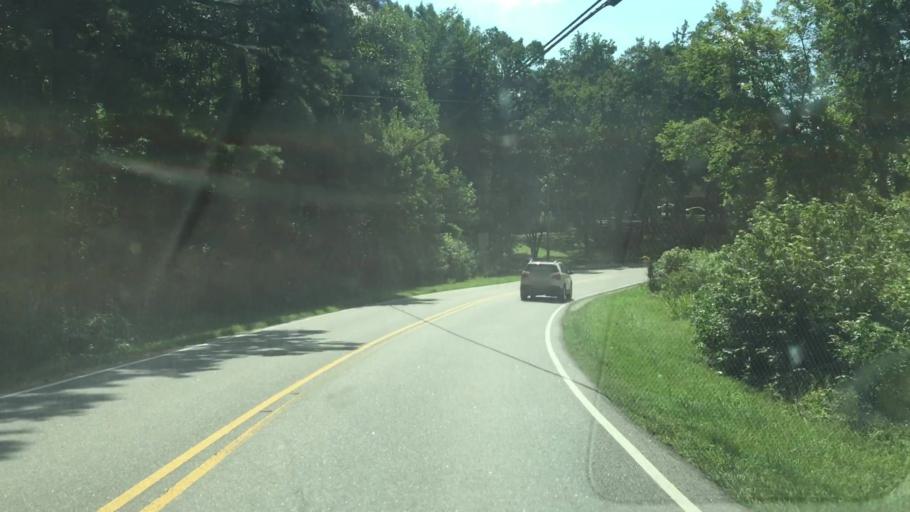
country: US
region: North Carolina
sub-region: Anson County
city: Polkton
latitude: 35.0100
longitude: -80.2108
